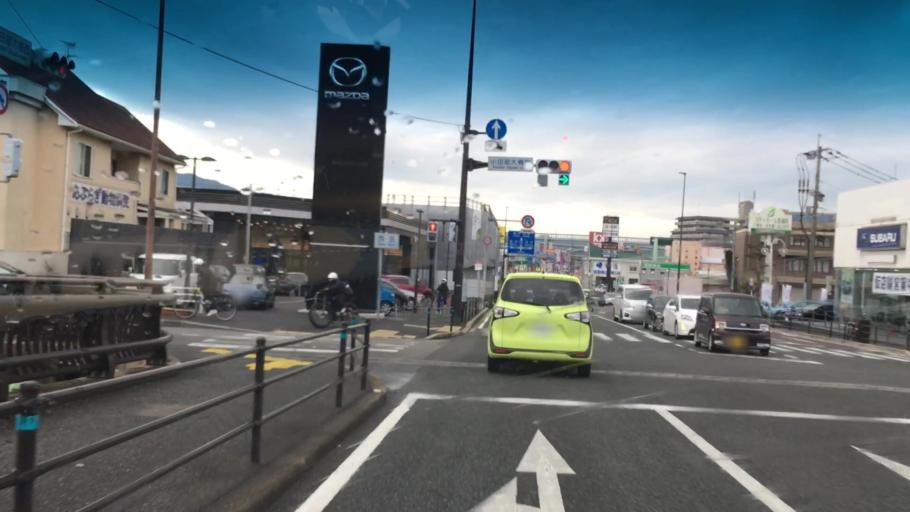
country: JP
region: Fukuoka
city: Fukuoka-shi
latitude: 33.5681
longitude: 130.3263
